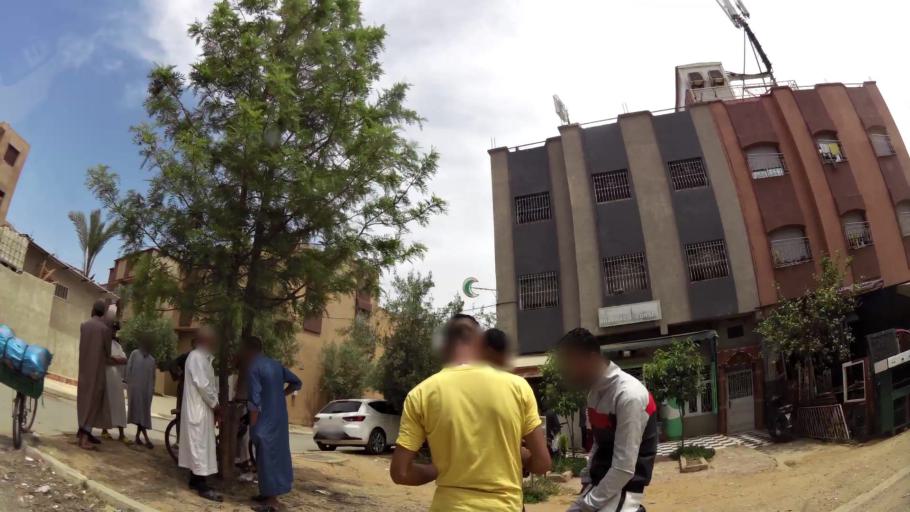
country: MA
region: Rabat-Sale-Zemmour-Zaer
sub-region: Khemisset
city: Khemisset
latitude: 33.8180
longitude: -6.0648
